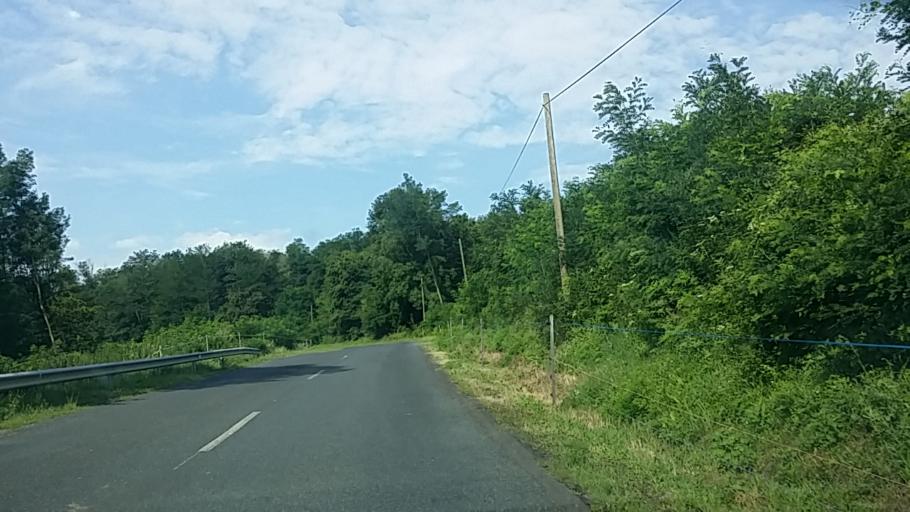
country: HU
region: Zala
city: Letenye
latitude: 46.5237
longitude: 16.7179
